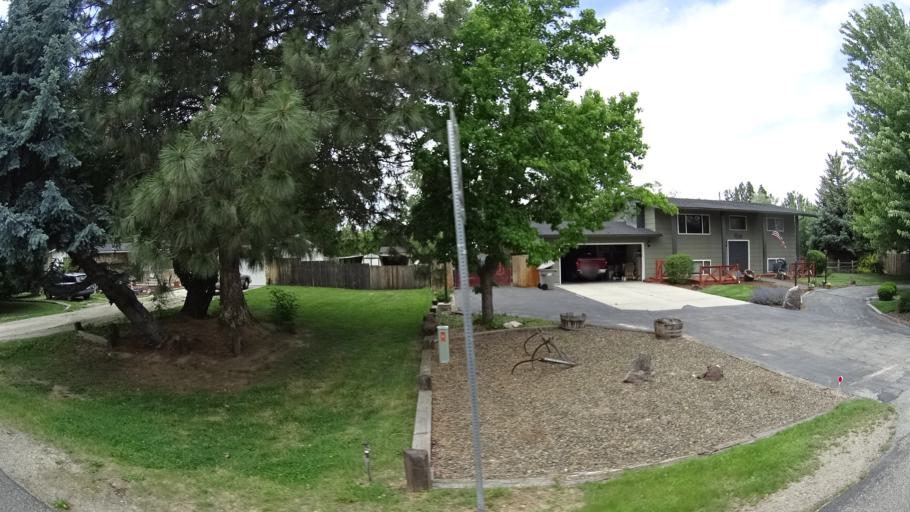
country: US
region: Idaho
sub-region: Ada County
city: Eagle
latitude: 43.6445
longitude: -116.3243
